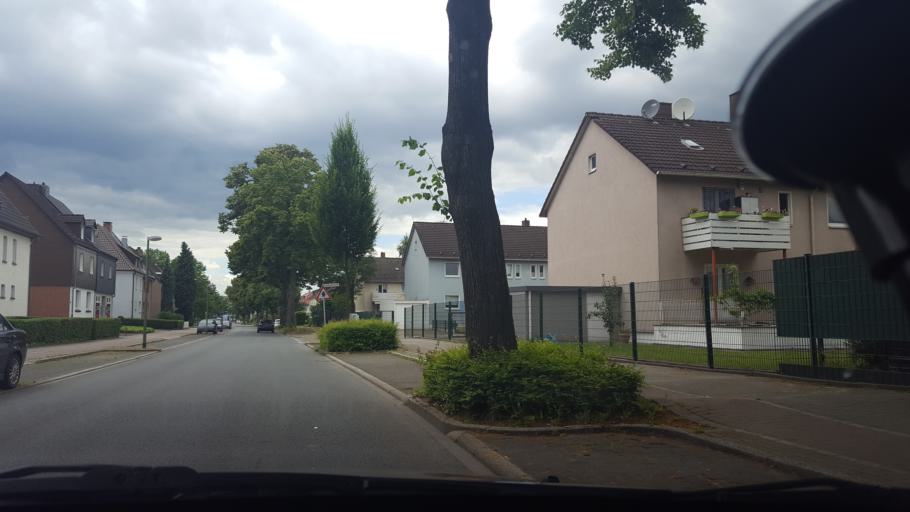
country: DE
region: North Rhine-Westphalia
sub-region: Regierungsbezirk Munster
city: Recklinghausen
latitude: 51.5968
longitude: 7.2115
